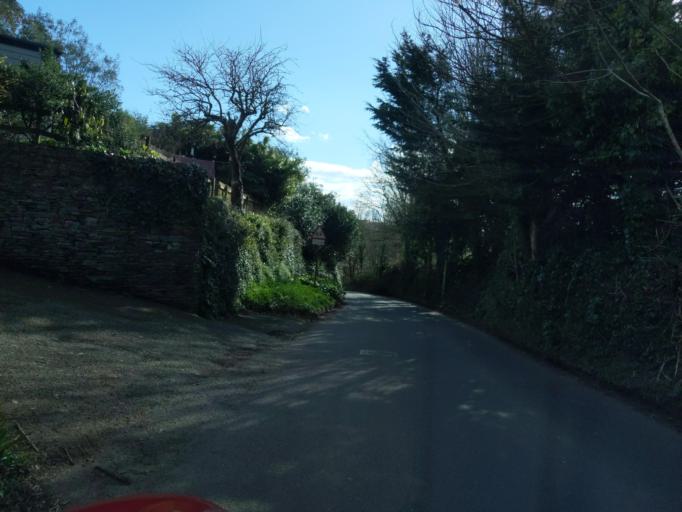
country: GB
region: England
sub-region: Devon
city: Kingsbridge
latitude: 50.2889
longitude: -3.7709
